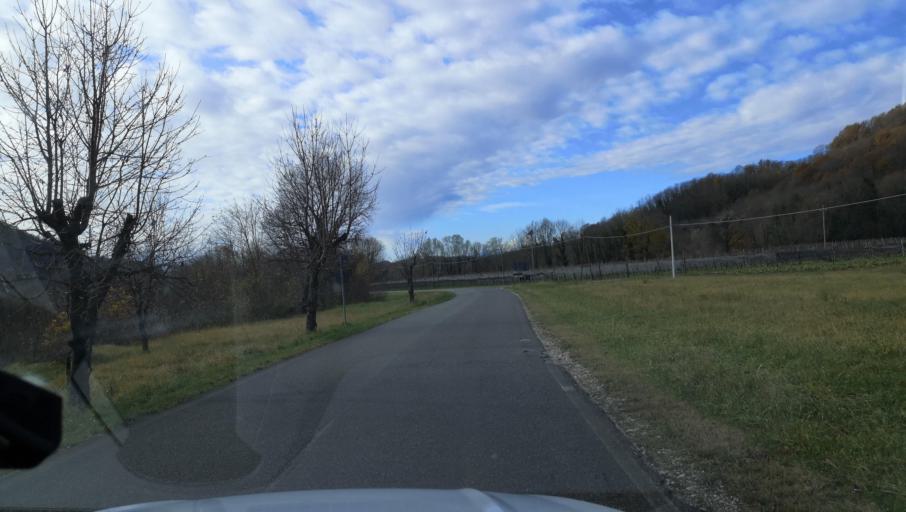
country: IT
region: Friuli Venezia Giulia
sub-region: Provincia di Udine
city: Nimis
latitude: 46.2038
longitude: 13.2893
